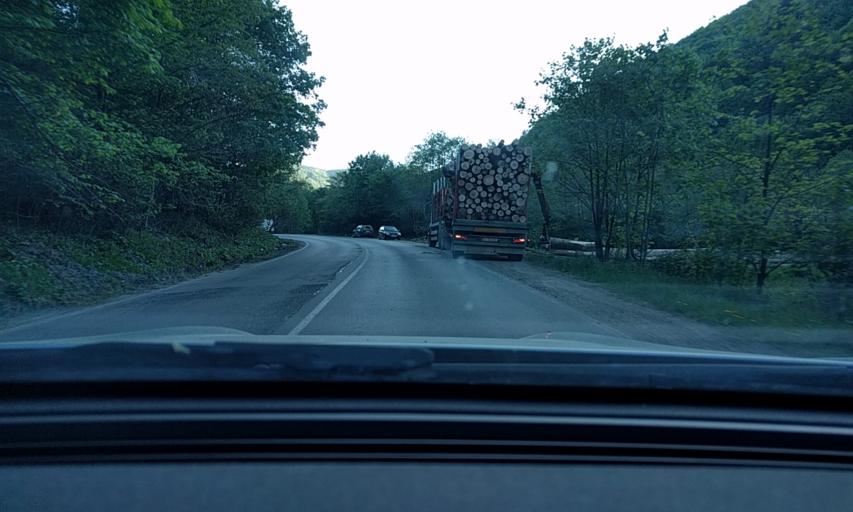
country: RO
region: Bacau
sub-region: Oras Slanic-Moldova
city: Slanic-Moldova
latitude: 46.1157
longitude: 26.4211
